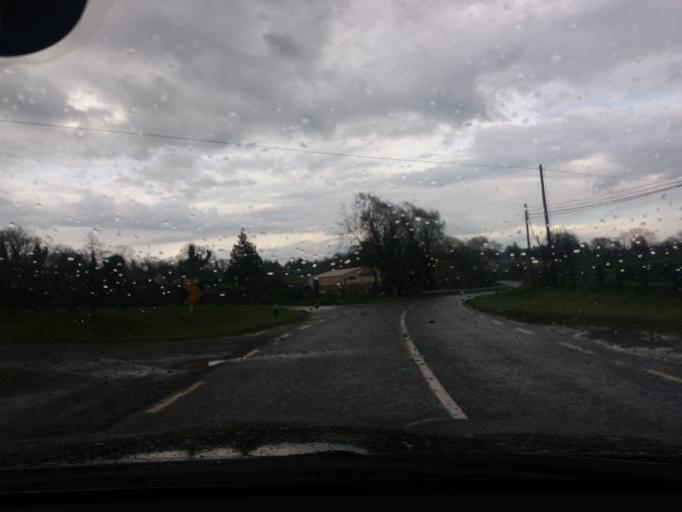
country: IE
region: Ulster
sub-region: An Cabhan
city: Ballyconnell
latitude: 54.1184
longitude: -7.6669
